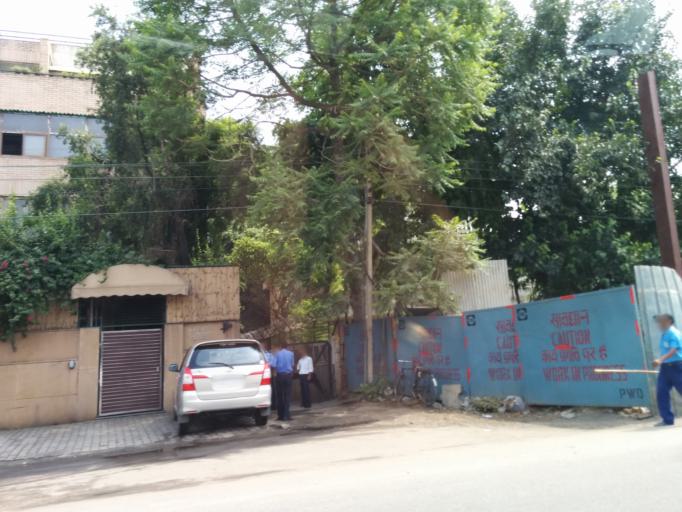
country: IN
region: NCT
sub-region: New Delhi
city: New Delhi
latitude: 28.5433
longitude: 77.2125
